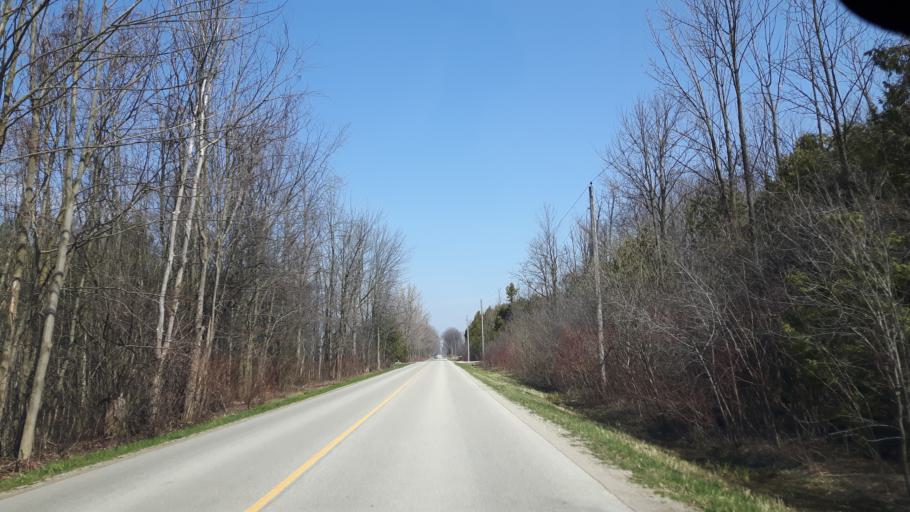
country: CA
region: Ontario
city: Goderich
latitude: 43.6878
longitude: -81.6847
